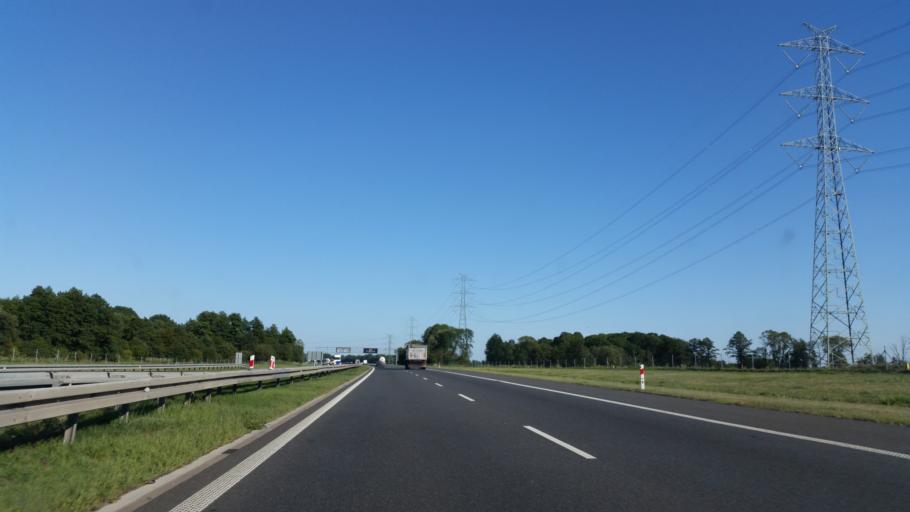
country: PL
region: Opole Voivodeship
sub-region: Powiat brzeski
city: Grodkow
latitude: 50.7773
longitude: 17.3580
